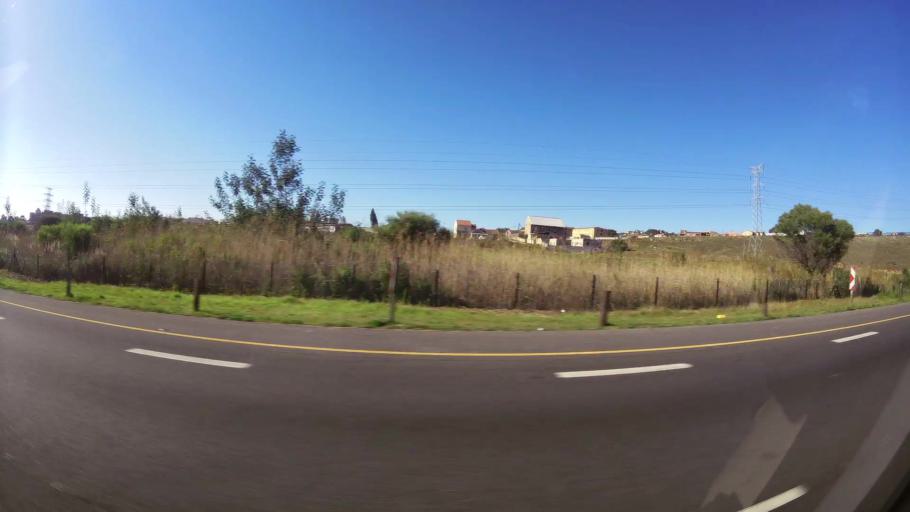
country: ZA
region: Eastern Cape
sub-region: Nelson Mandela Bay Metropolitan Municipality
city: Port Elizabeth
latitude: -33.9256
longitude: 25.5619
